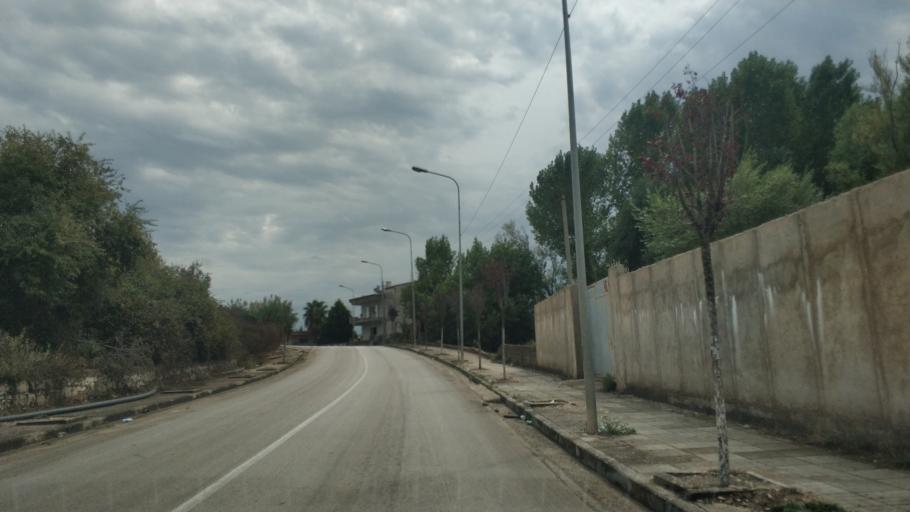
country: AL
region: Vlore
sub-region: Rrethi i Sarandes
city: Sarande
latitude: 39.8424
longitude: 20.0352
